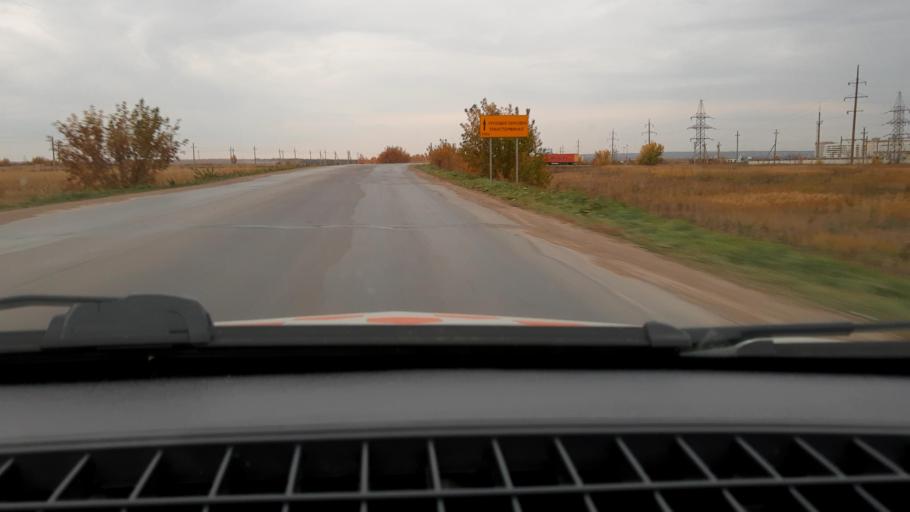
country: RU
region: Bashkortostan
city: Iglino
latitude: 54.7623
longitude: 56.2619
